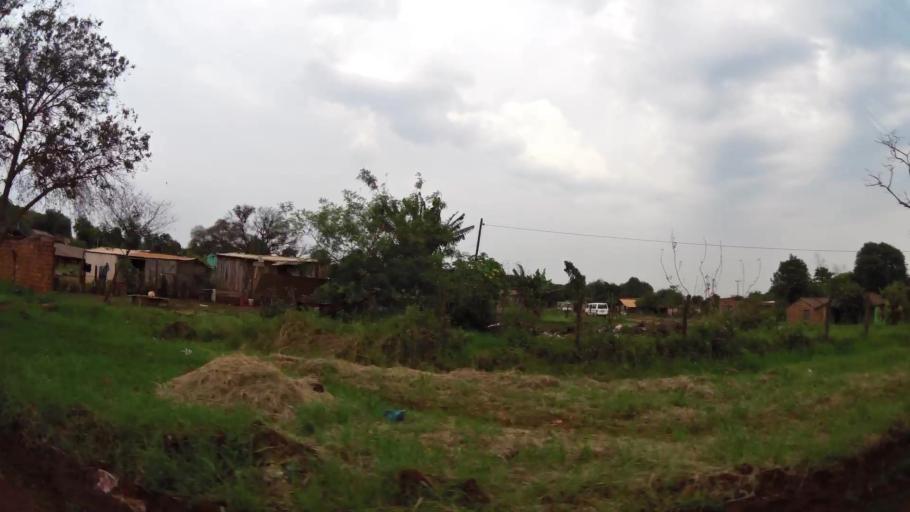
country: PY
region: Alto Parana
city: Presidente Franco
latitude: -25.5445
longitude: -54.6529
